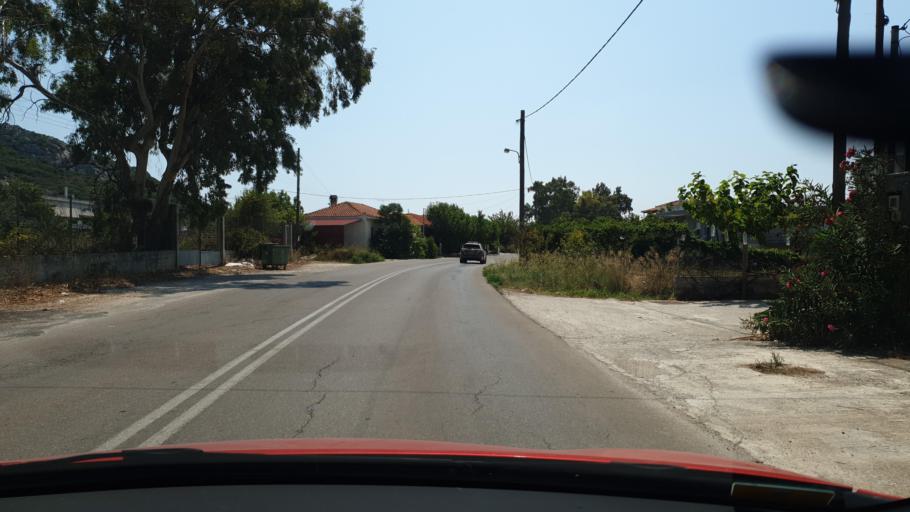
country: GR
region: Central Greece
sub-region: Nomos Evvoias
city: Oxilithos
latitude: 38.4806
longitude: 24.1184
